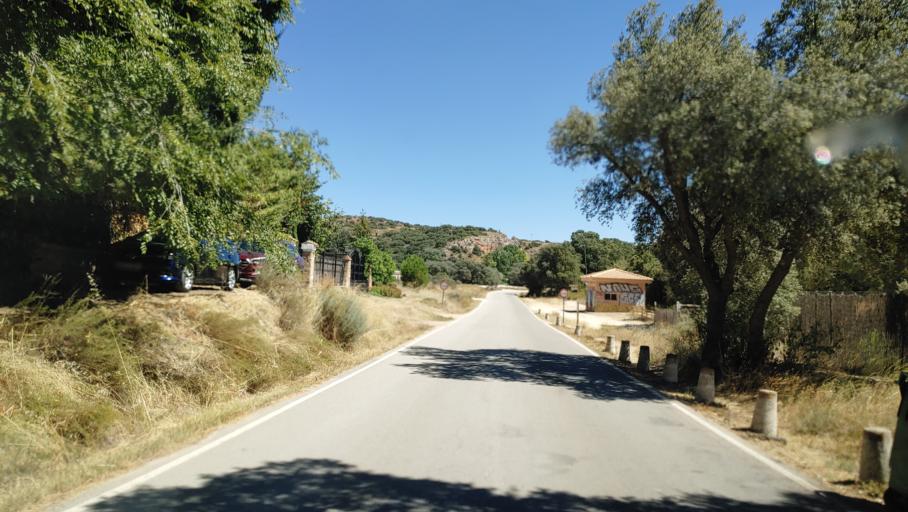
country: ES
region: Castille-La Mancha
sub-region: Provincia de Ciudad Real
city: Ruidera
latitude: 38.9353
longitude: -2.8460
